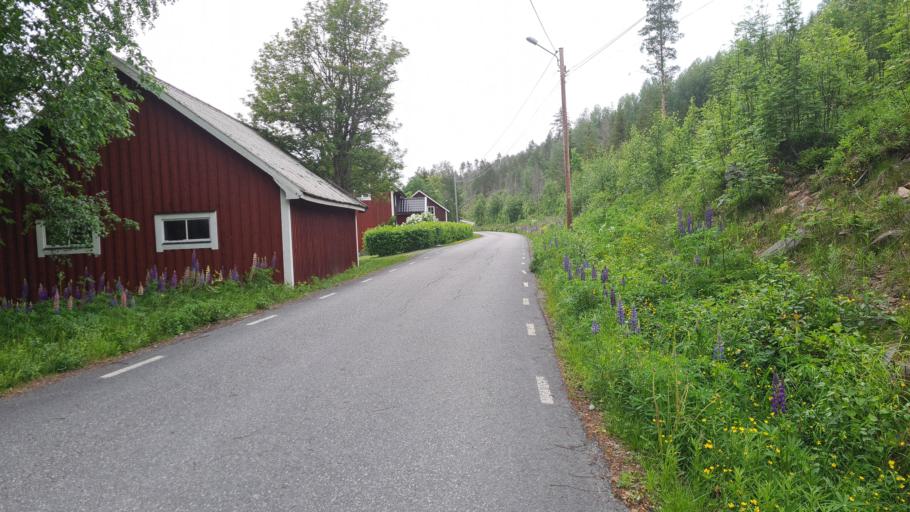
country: SE
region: Vaesternorrland
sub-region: Kramfors Kommun
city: Nordingra
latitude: 62.9749
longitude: 18.4246
